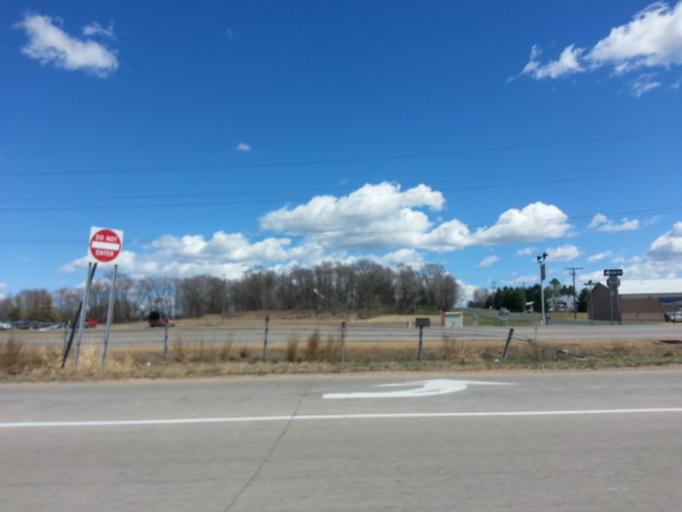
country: US
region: Minnesota
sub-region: Dakota County
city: Hastings
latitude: 44.7759
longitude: -92.8634
